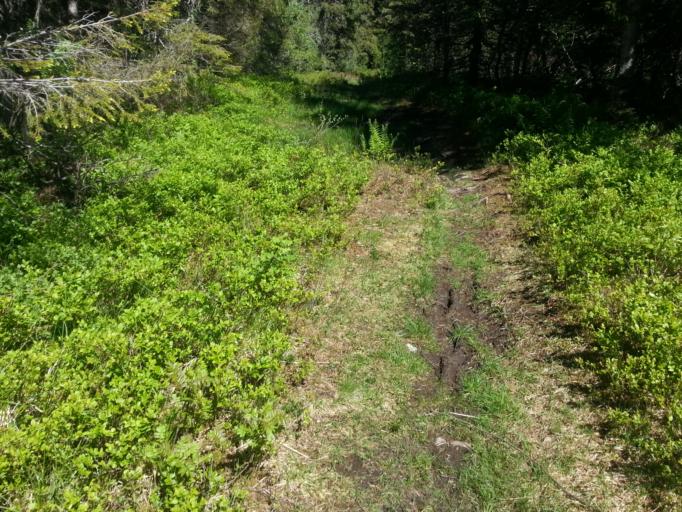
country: NO
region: Sor-Trondelag
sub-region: Trondheim
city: Trondheim
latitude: 63.4058
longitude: 10.2874
